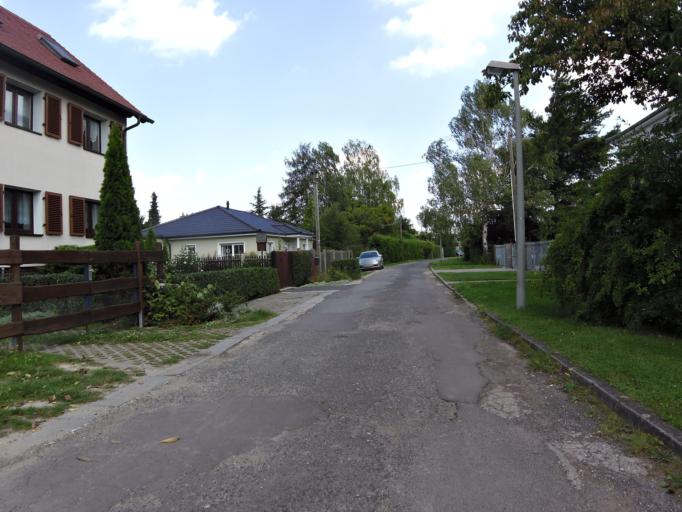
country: DE
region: Saxony
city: Leipzig
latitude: 51.3845
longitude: 12.3482
